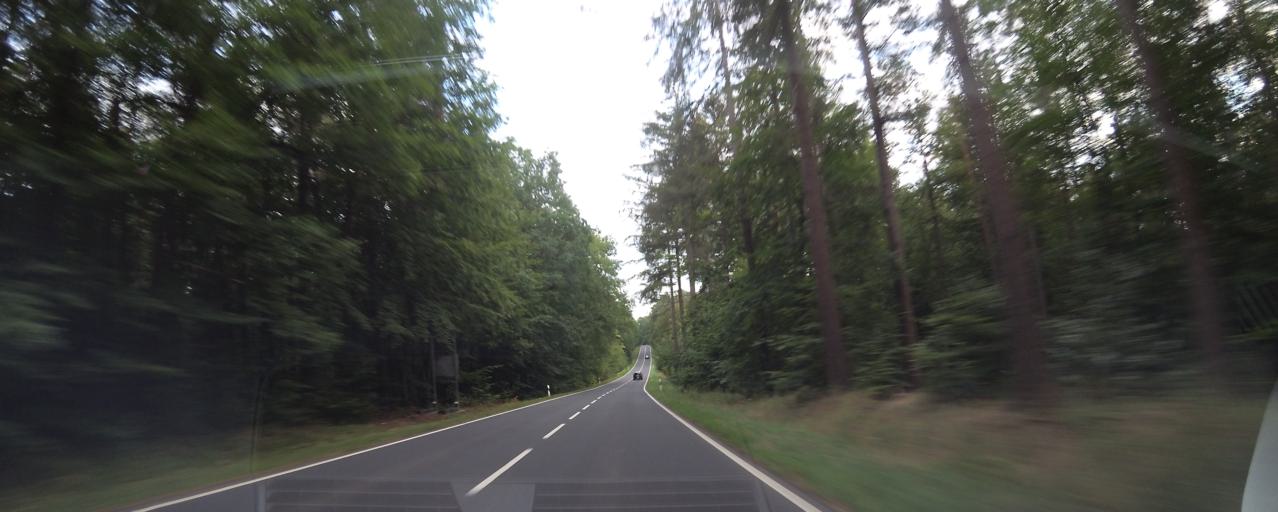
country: DE
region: Rheinland-Pfalz
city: Zemmer
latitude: 49.9135
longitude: 6.7070
